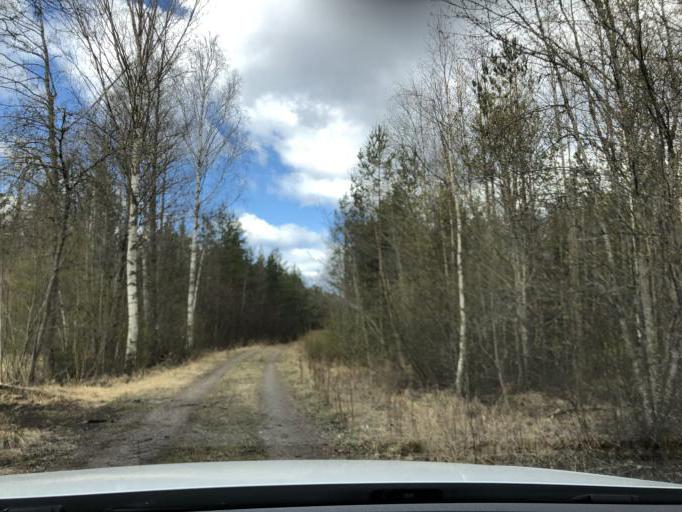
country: SE
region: Uppsala
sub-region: Tierps Kommun
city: Tierp
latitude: 60.3276
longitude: 17.3514
